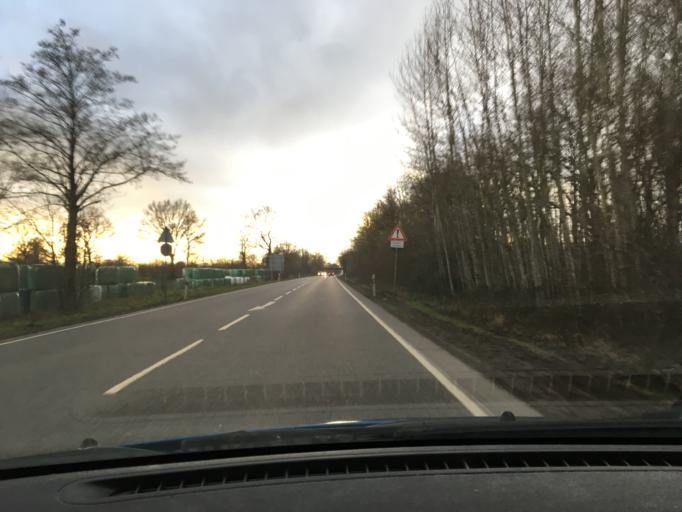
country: DE
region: Schleswig-Holstein
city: Klein Offenseth-Sparrieshoop
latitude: 53.8107
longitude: 9.6938
